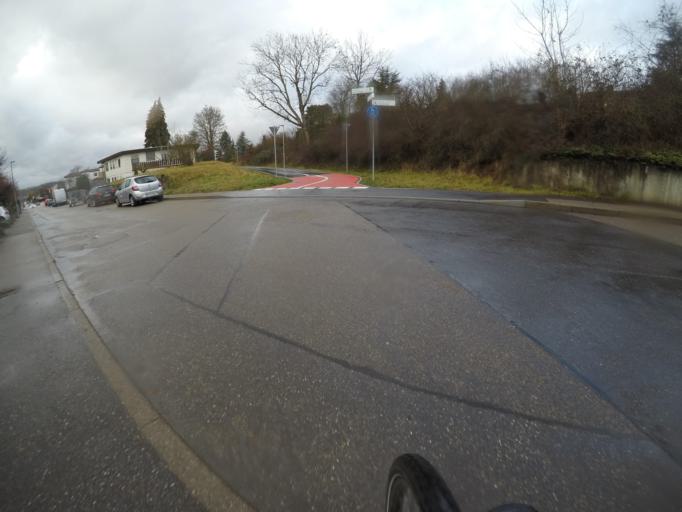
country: DE
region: Baden-Wuerttemberg
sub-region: Regierungsbezirk Stuttgart
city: Vaihingen an der Enz
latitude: 48.9303
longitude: 8.9694
